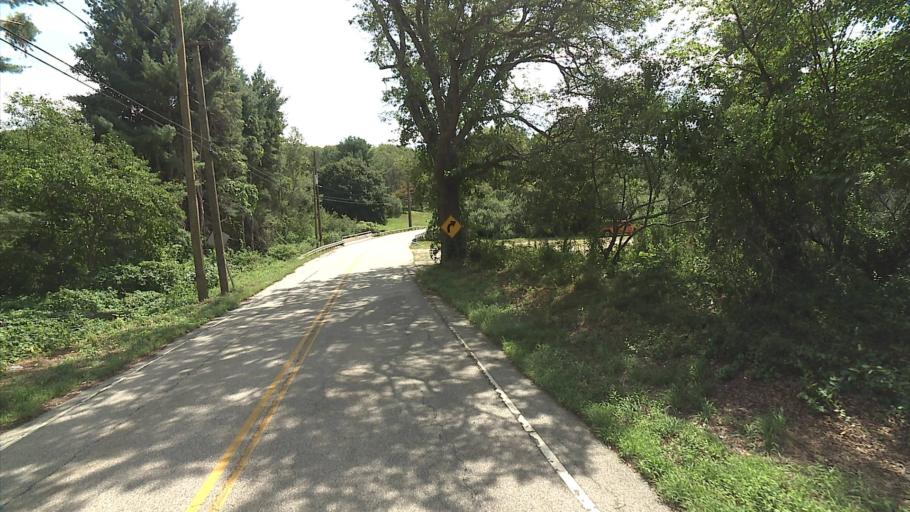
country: US
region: Connecticut
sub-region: New London County
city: Lisbon
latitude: 41.6124
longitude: -72.0359
